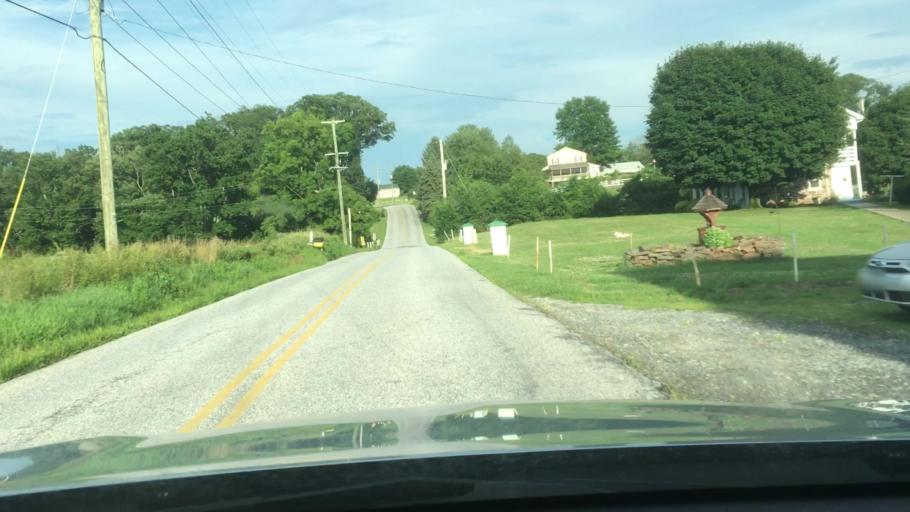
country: US
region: Pennsylvania
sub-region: York County
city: Dover
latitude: 40.0260
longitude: -76.8384
